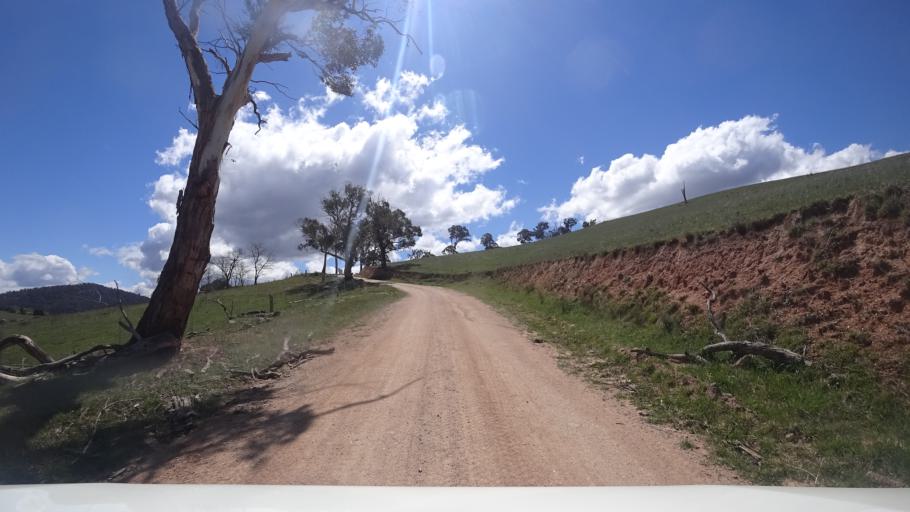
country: AU
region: New South Wales
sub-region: Oberon
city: Oberon
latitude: -33.5739
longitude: 149.9414
